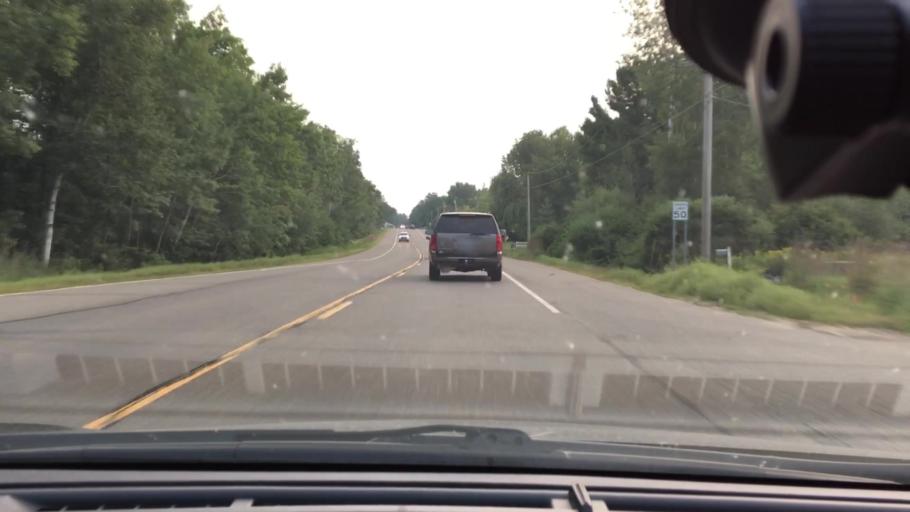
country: US
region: Minnesota
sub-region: Crow Wing County
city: Crosby
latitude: 46.4897
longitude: -93.9275
